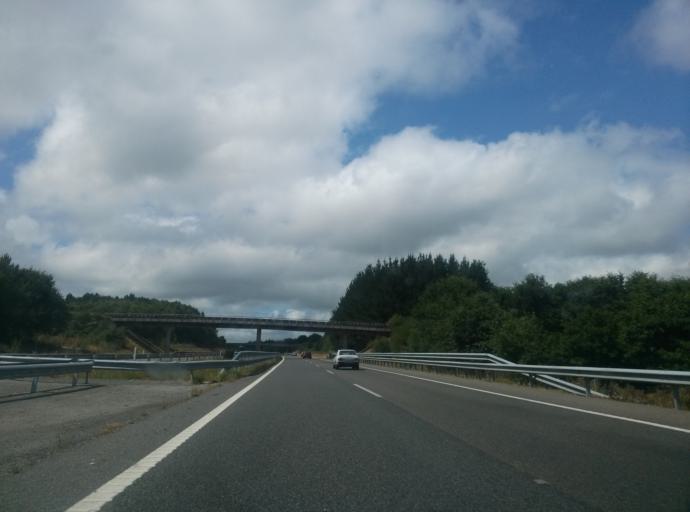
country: ES
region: Galicia
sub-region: Provincia de Lugo
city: Outeiro de Rei
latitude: 43.0810
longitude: -7.5797
